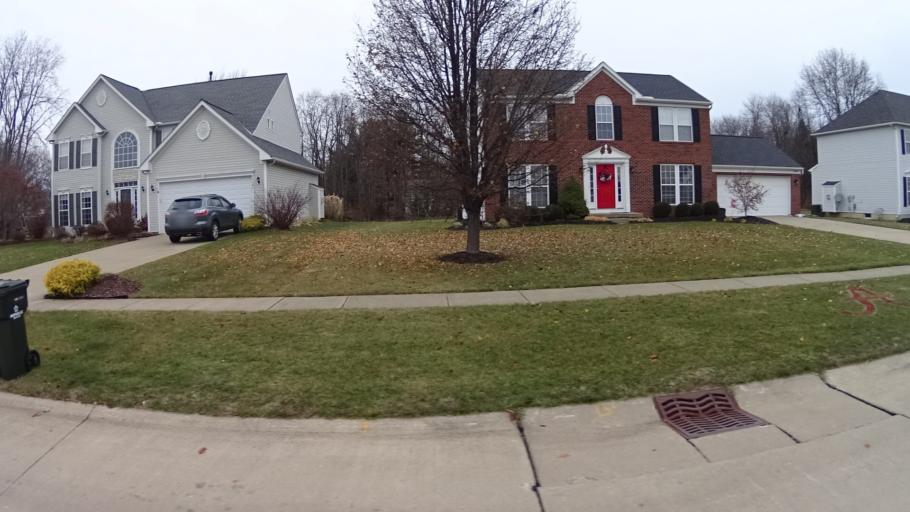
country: US
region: Ohio
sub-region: Lorain County
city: North Ridgeville
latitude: 41.3621
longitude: -82.0012
